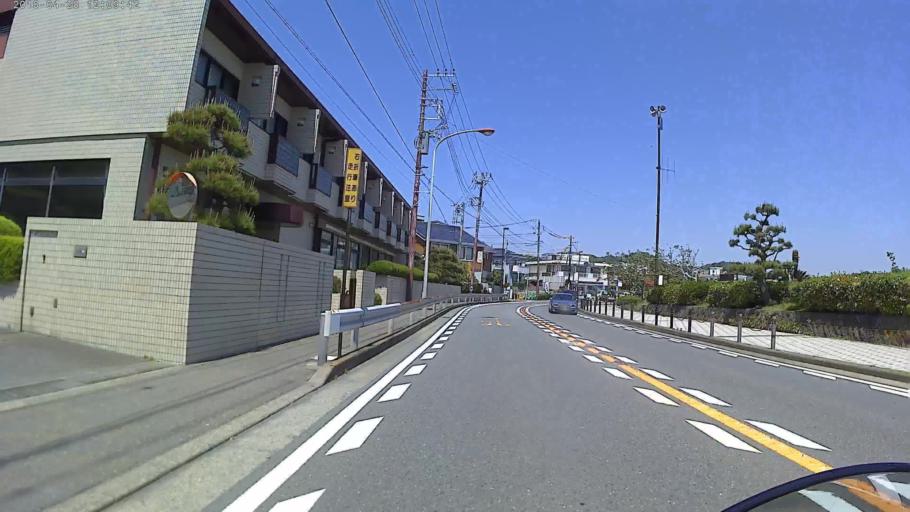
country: JP
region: Kanagawa
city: Kamakura
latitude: 35.3079
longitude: 139.5335
